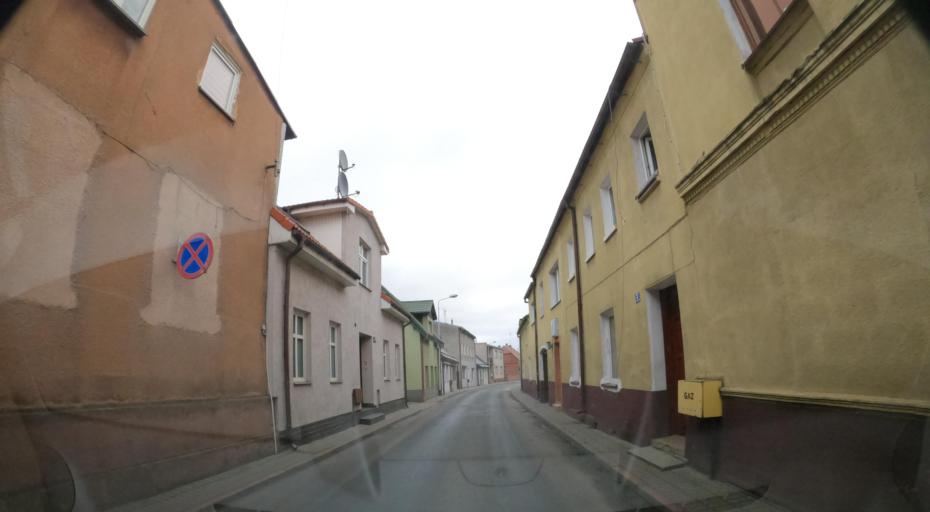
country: PL
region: Greater Poland Voivodeship
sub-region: Powiat pilski
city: Lobzenica
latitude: 53.2595
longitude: 17.2554
